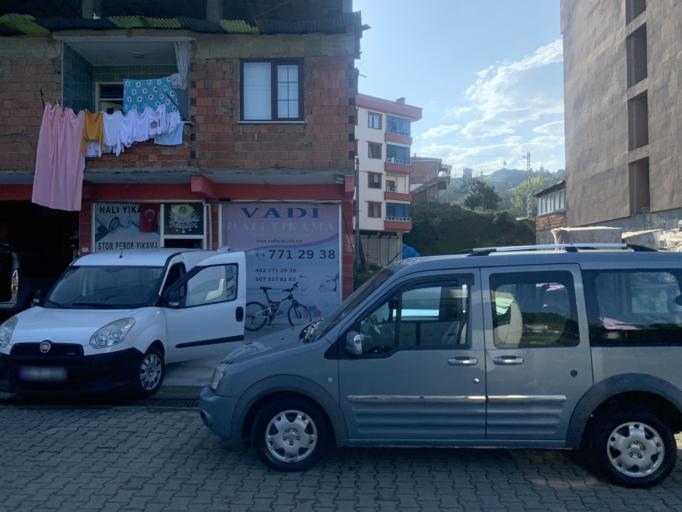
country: TR
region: Trabzon
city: Of
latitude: 40.9393
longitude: 40.2711
